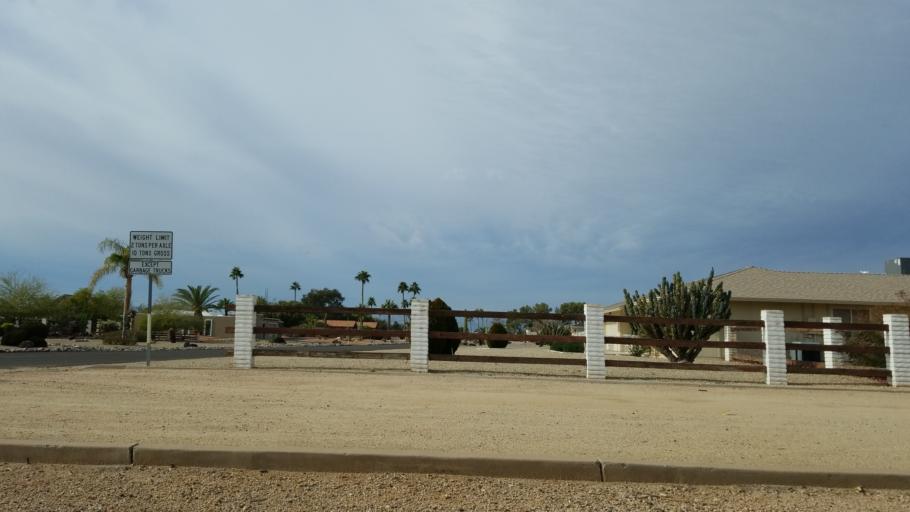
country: US
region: Arizona
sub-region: Maricopa County
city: Youngtown
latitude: 33.5770
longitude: -112.2988
